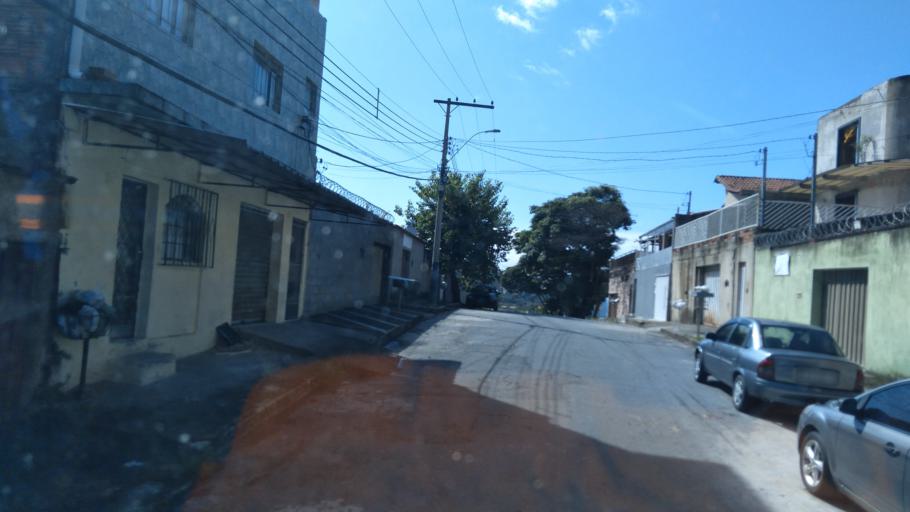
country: BR
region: Minas Gerais
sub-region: Santa Luzia
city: Santa Luzia
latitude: -19.8248
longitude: -43.8999
